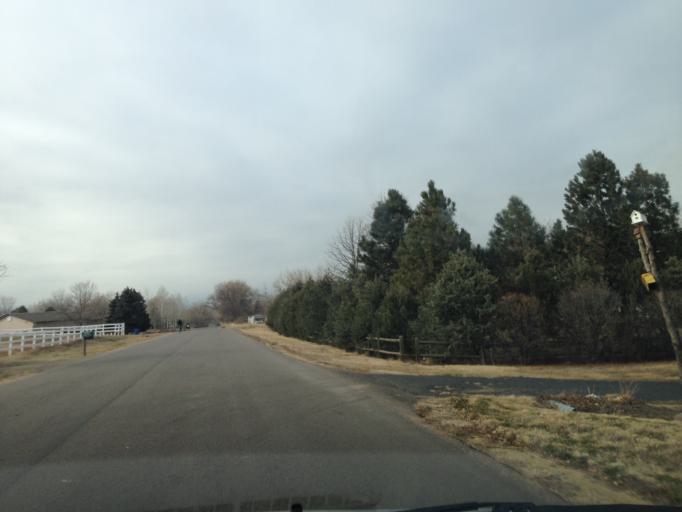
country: US
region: Colorado
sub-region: Boulder County
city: Erie
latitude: 40.0449
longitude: -105.0799
